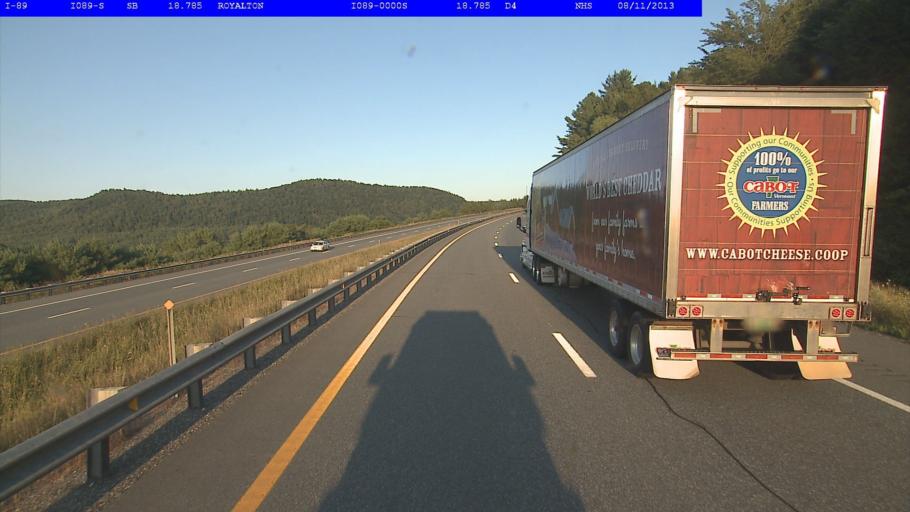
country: US
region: Vermont
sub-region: Orange County
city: Randolph
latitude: 43.8227
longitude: -72.5317
